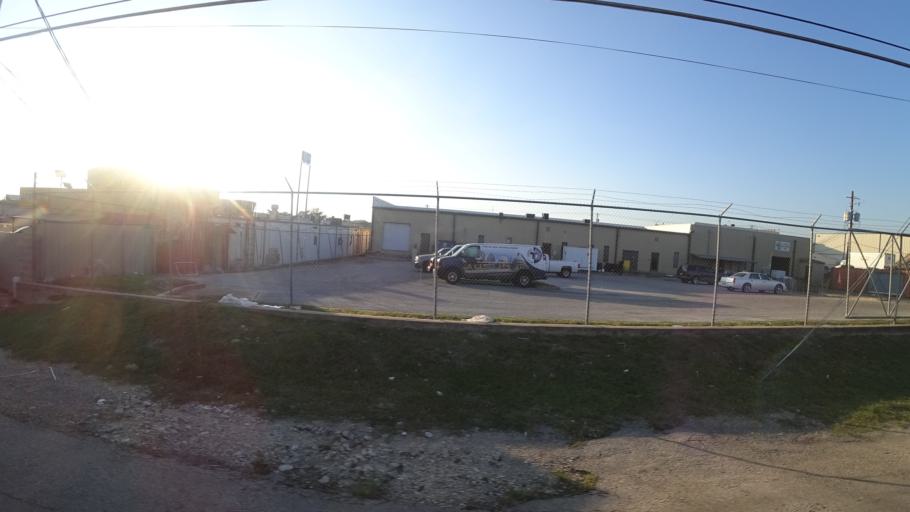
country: US
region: Texas
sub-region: Travis County
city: Wells Branch
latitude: 30.3583
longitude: -97.6860
